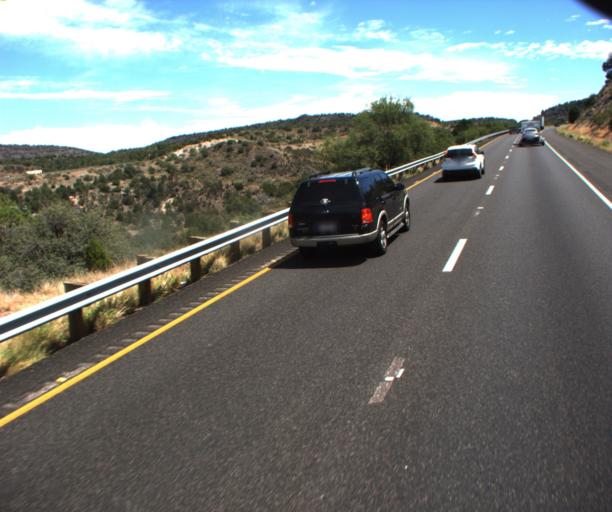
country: US
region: Arizona
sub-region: Yavapai County
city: Big Park
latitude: 34.7051
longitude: -111.7374
